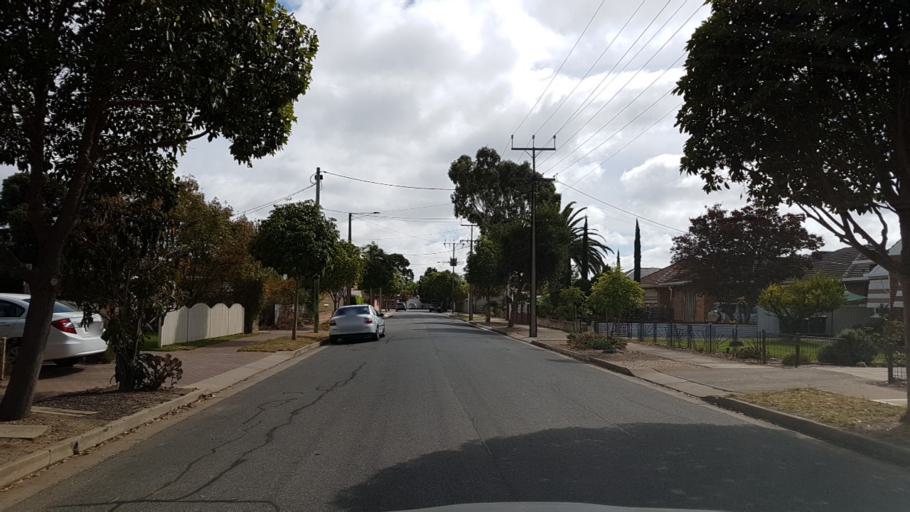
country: AU
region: South Australia
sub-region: Marion
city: Plympton Park
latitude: -34.9820
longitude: 138.5525
